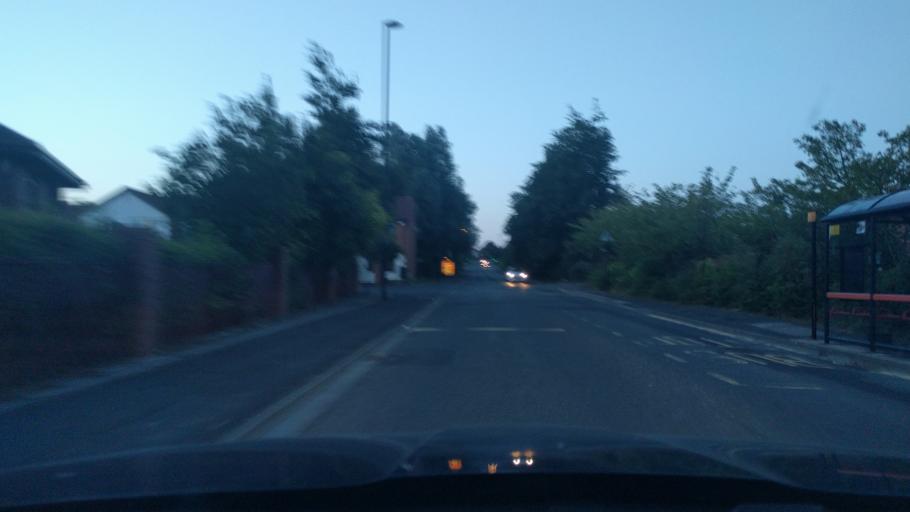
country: GB
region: England
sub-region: Northumberland
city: Seghill
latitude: 55.0356
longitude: -1.5702
